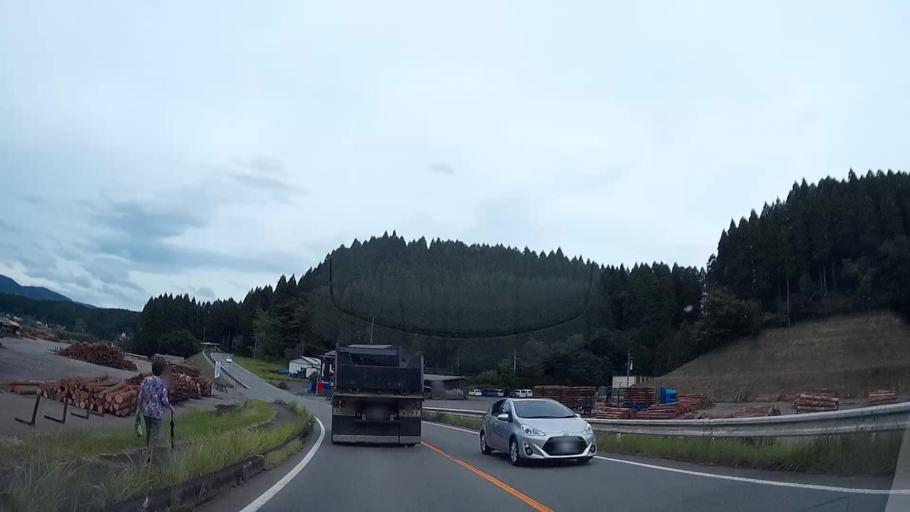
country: JP
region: Oita
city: Tsukawaki
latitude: 33.1254
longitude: 131.0571
